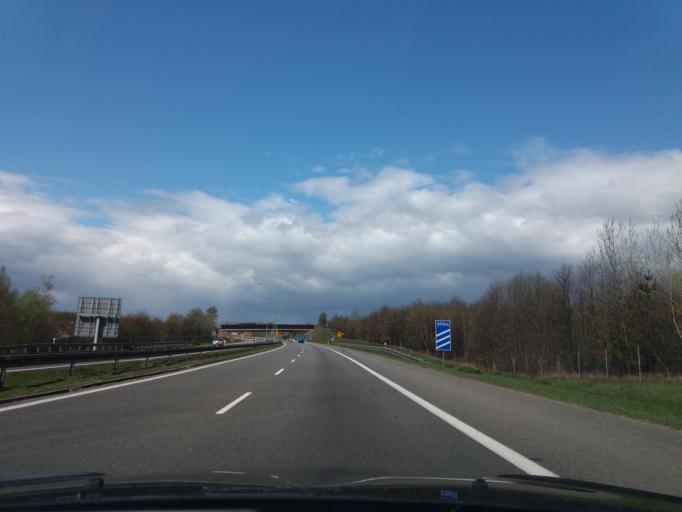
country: PL
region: Opole Voivodeship
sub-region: Powiat strzelecki
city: Ujazd
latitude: 50.4428
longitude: 18.3569
